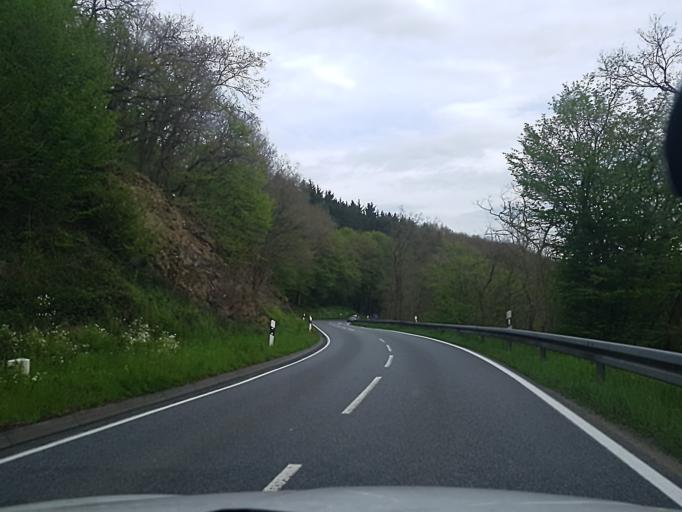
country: DE
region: Hesse
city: Bad Camberg
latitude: 50.2873
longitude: 8.2252
